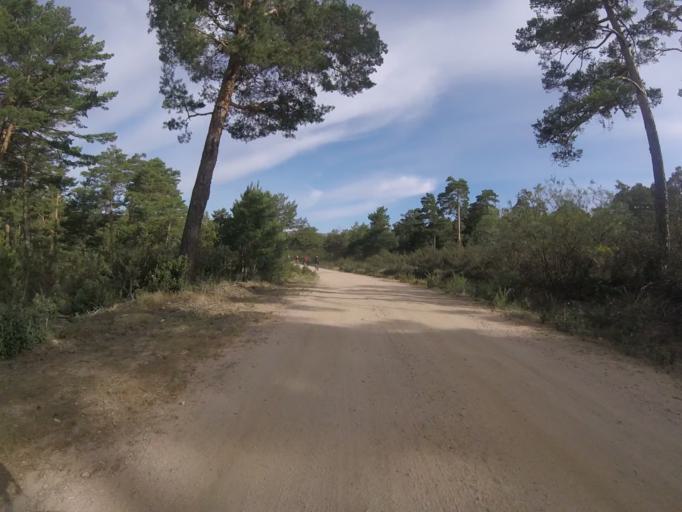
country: ES
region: Castille and Leon
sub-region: Provincia de Avila
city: Peguerinos
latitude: 40.6503
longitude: -4.1781
